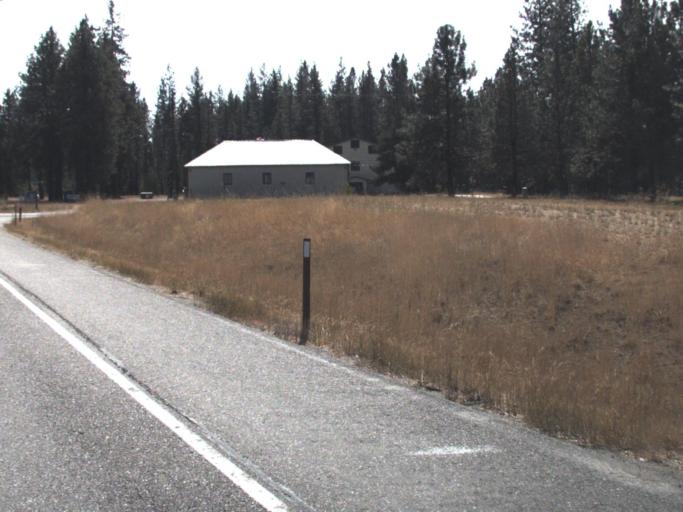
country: US
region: Washington
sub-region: Stevens County
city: Chewelah
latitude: 48.1580
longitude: -117.6929
